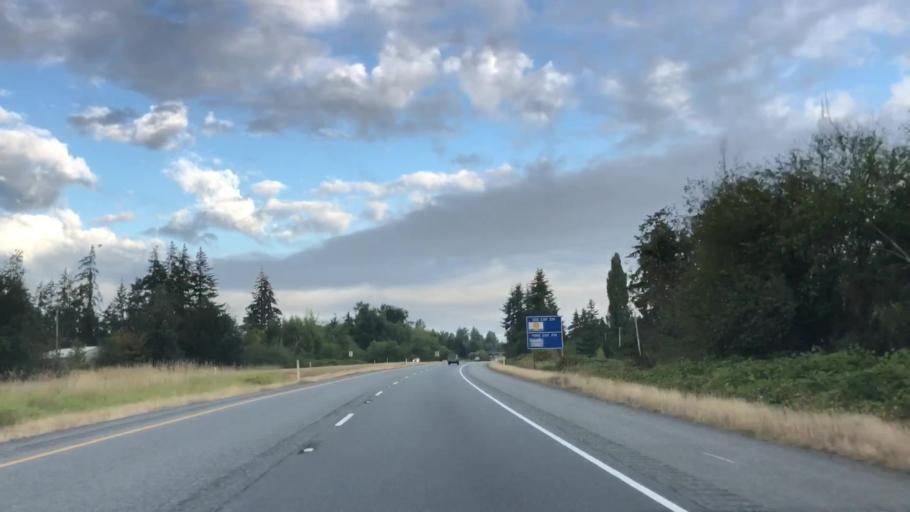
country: US
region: Washington
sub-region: Whatcom County
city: Blaine
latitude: 48.9699
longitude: -122.7167
